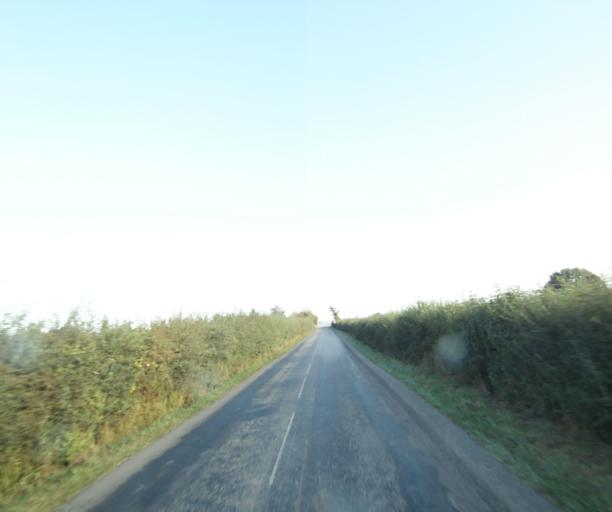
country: FR
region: Bourgogne
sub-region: Departement de Saone-et-Loire
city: Palinges
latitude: 46.5625
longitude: 4.1845
